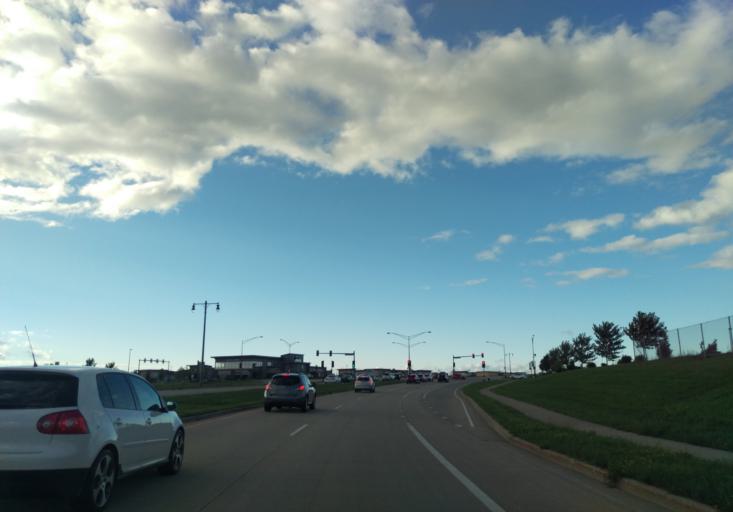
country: US
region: Wisconsin
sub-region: Dane County
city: Sun Prairie
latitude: 43.1646
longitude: -89.2688
